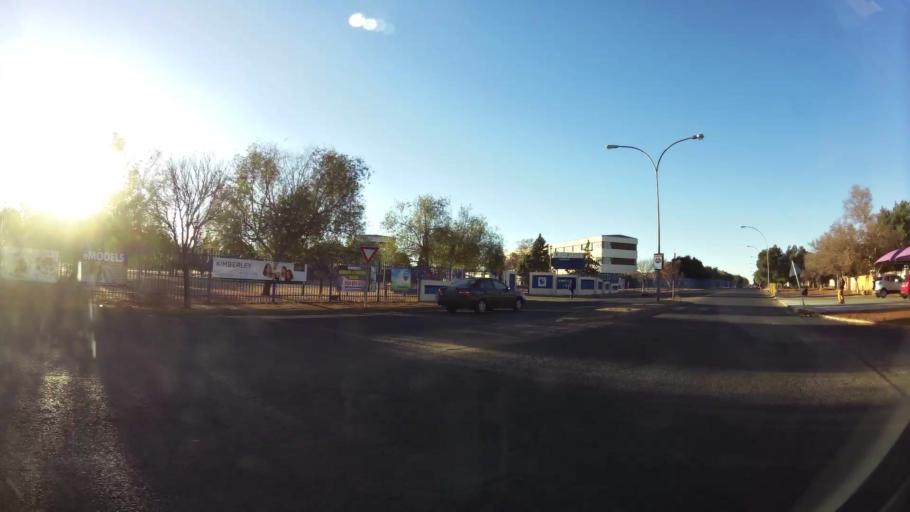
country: ZA
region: Northern Cape
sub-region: Frances Baard District Municipality
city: Kimberley
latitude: -28.7535
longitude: 24.7456
